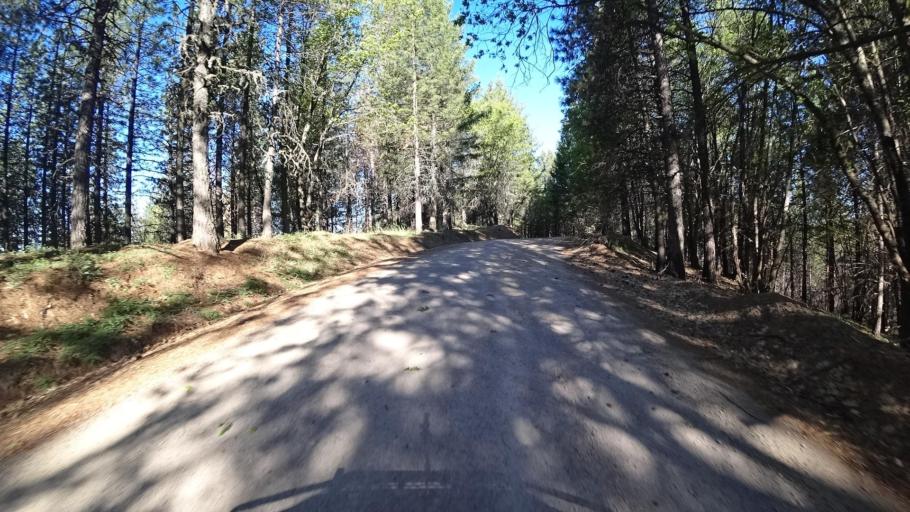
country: US
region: California
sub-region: Lake County
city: Upper Lake
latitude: 39.3498
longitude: -122.9708
